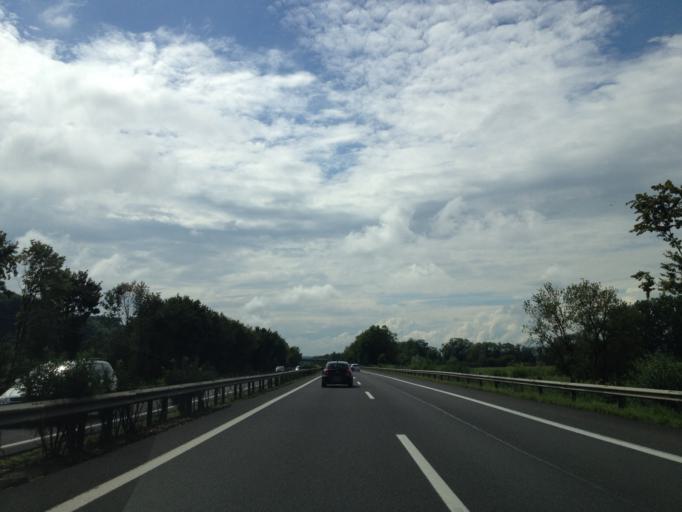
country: AT
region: Styria
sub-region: Politischer Bezirk Hartberg-Fuerstenfeld
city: Ilz
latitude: 47.0800
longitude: 15.9279
